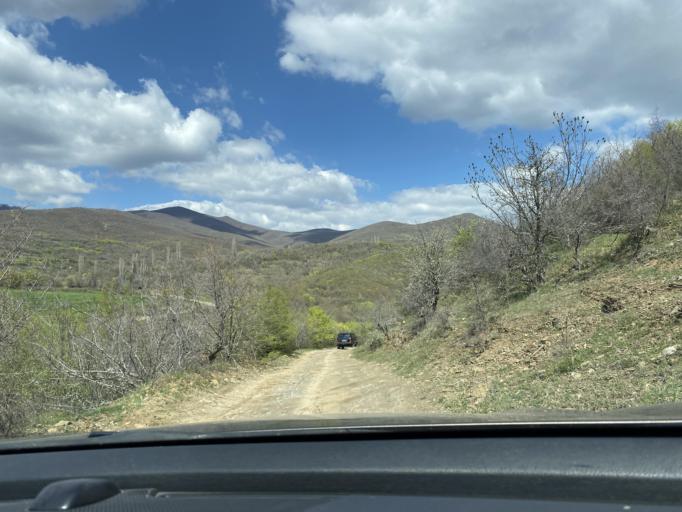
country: MK
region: Caska
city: Caska
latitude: 41.7339
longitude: 21.6495
